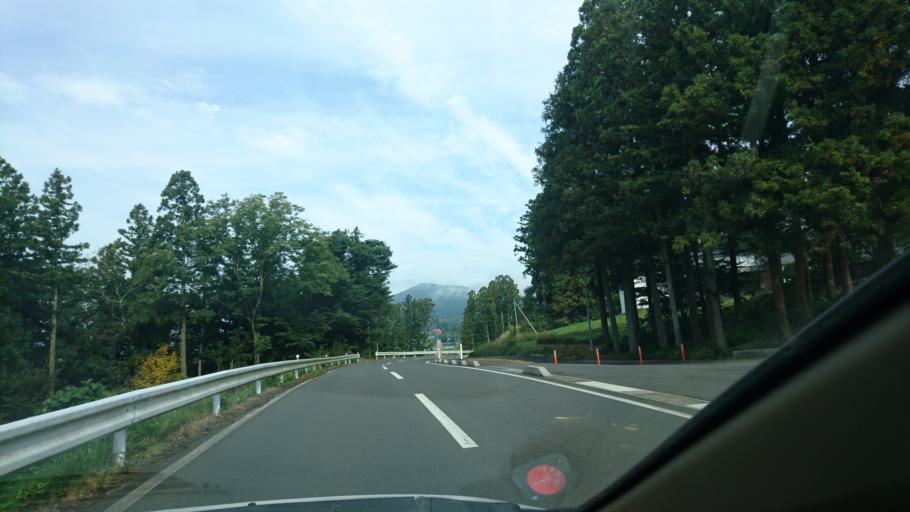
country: JP
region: Iwate
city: Ichinoseki
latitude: 38.9549
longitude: 141.1716
